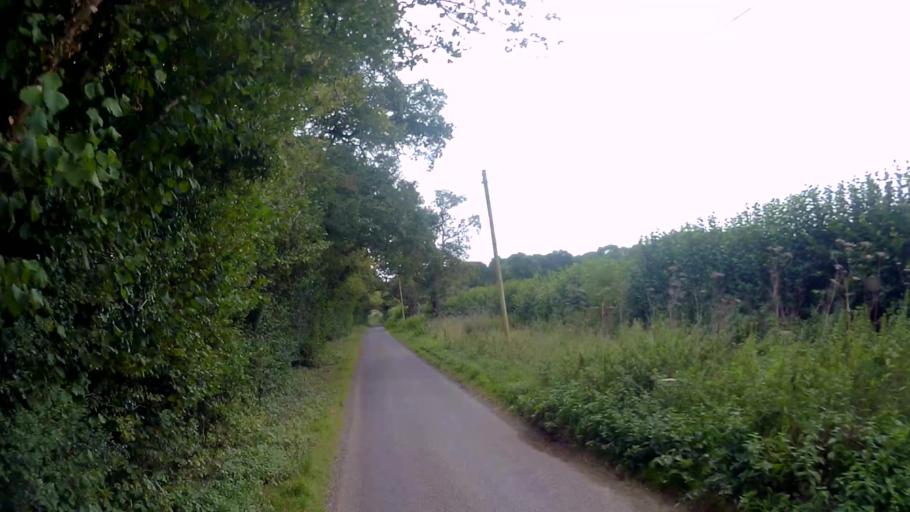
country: GB
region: England
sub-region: Hampshire
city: Overton
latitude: 51.2141
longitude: -1.2279
